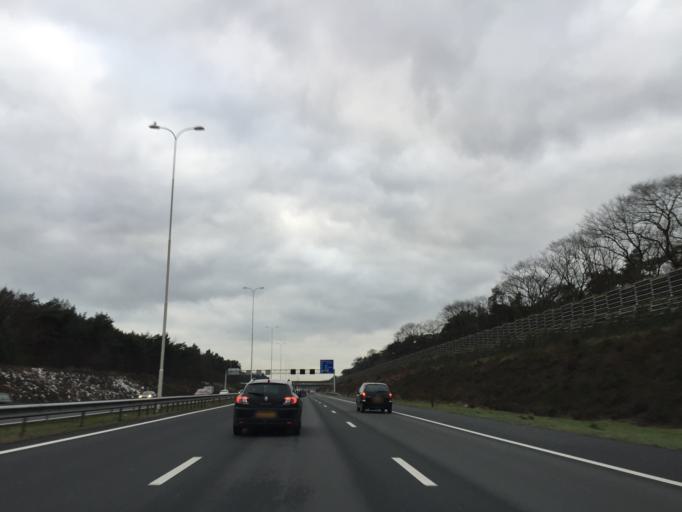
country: NL
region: Utrecht
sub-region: Gemeente Zeist
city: Zeist
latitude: 52.1113
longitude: 5.2811
